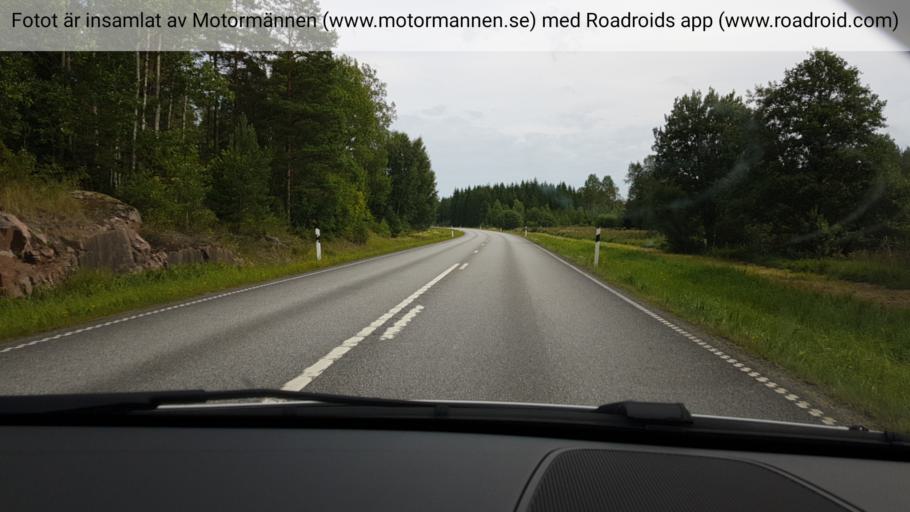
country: SE
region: Stockholm
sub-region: Norrtalje Kommun
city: Hallstavik
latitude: 60.0882
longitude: 18.4859
